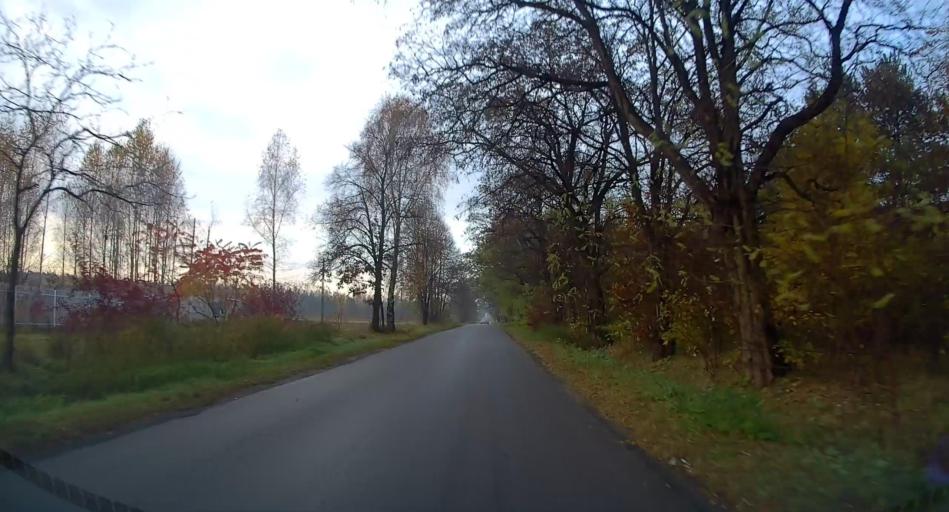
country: PL
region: Masovian Voivodeship
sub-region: Powiat zyrardowski
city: Puszcza Marianska
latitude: 51.9317
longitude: 20.3623
